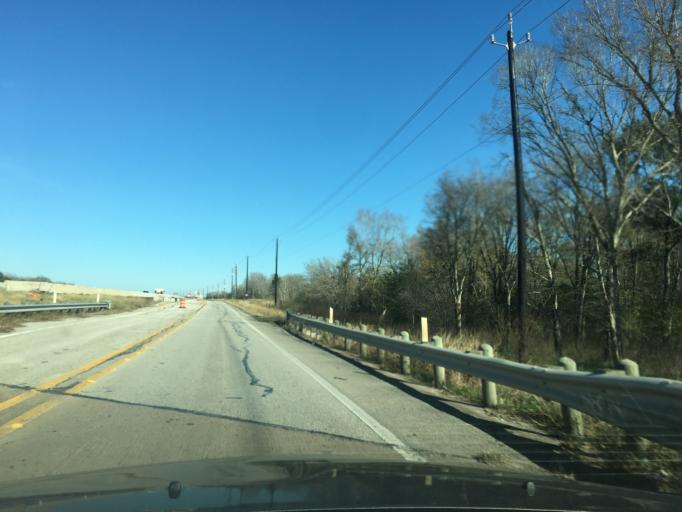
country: US
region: Texas
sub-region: Wharton County
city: East Bernard
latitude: 29.4491
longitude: -95.9931
